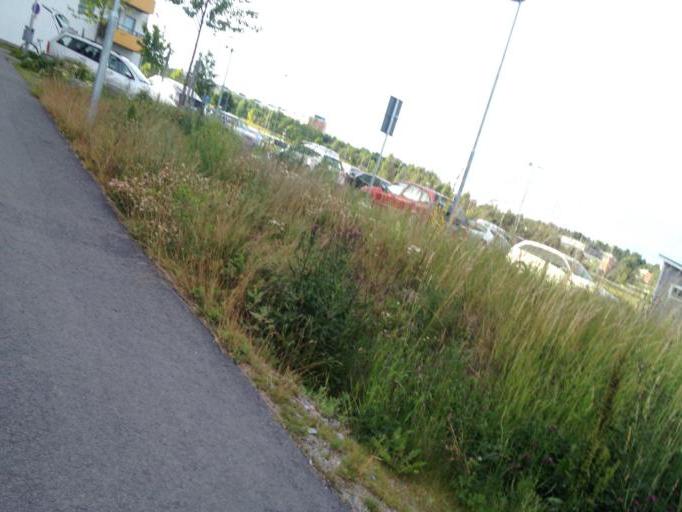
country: SE
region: Stockholm
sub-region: Sigtuna Kommun
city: Marsta
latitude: 59.6150
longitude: 17.8471
